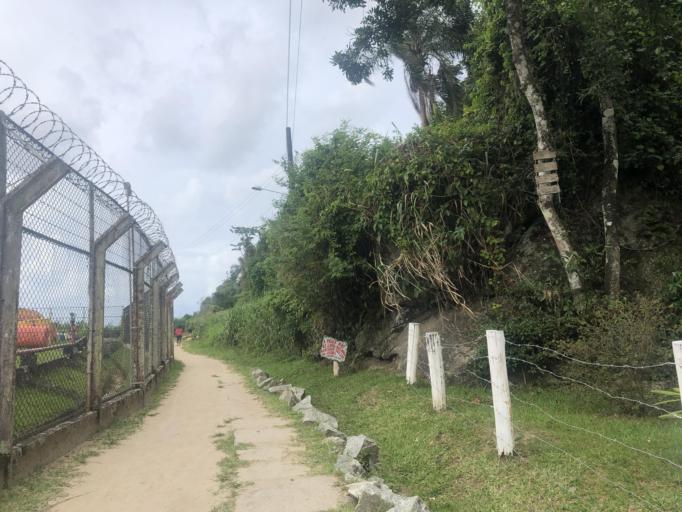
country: BR
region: Santa Catarina
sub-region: Sao Francisco Do Sul
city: Sao Francisco do Sul
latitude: -26.2194
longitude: -48.4979
